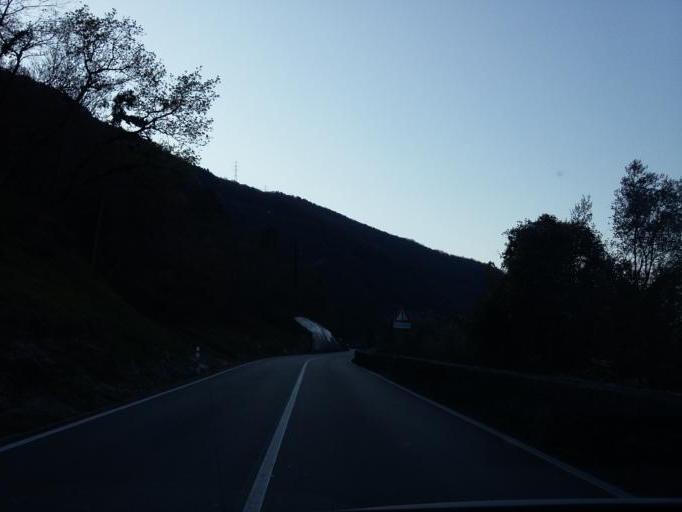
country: IT
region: Trentino-Alto Adige
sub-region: Provincia di Trento
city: Bolognano-Vignole
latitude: 45.8959
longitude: 10.8960
